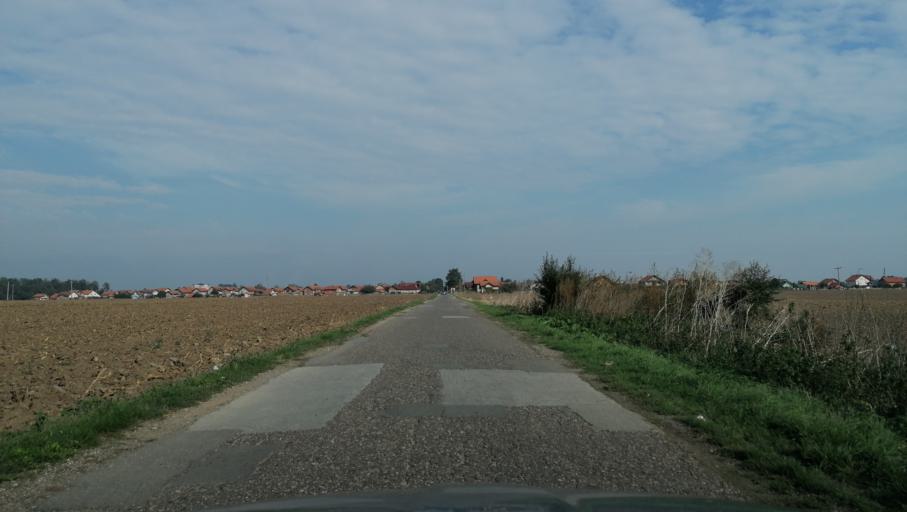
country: BA
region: Republika Srpska
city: Popovi
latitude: 44.7738
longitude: 19.2625
